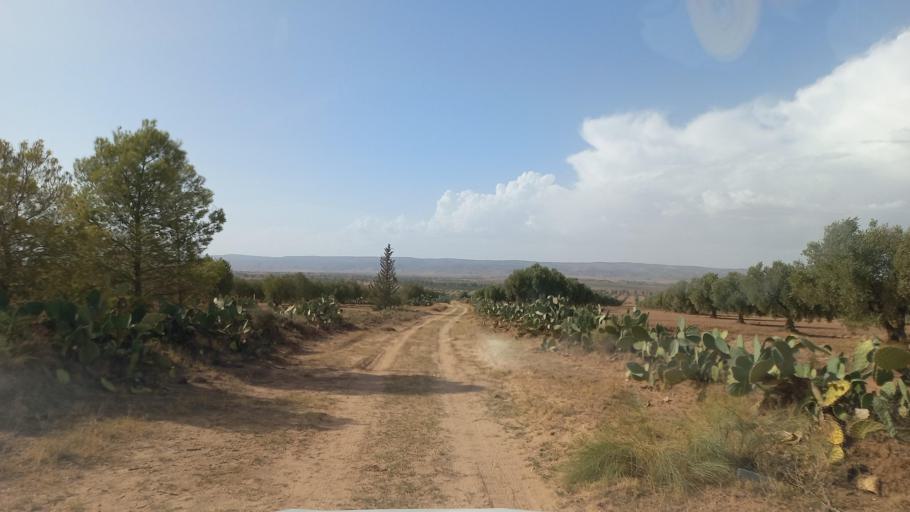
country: TN
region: Al Qasrayn
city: Kasserine
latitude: 35.2106
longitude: 8.9546
